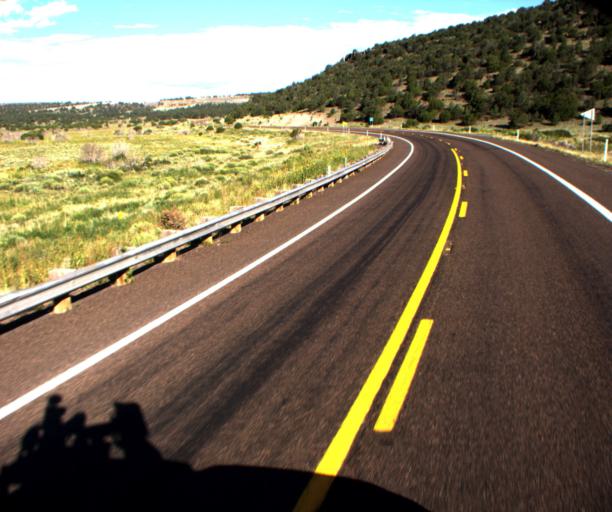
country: US
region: Arizona
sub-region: Apache County
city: Eagar
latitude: 34.0918
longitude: -109.2037
